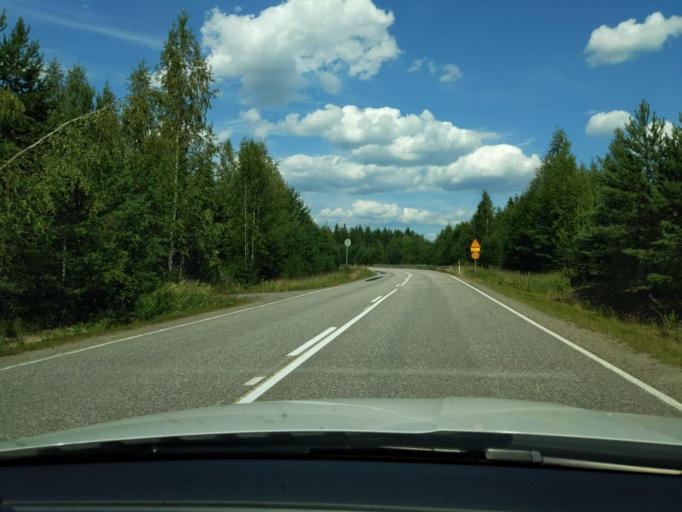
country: FI
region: Paijanne Tavastia
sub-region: Lahti
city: Heinola
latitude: 61.3269
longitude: 26.1563
